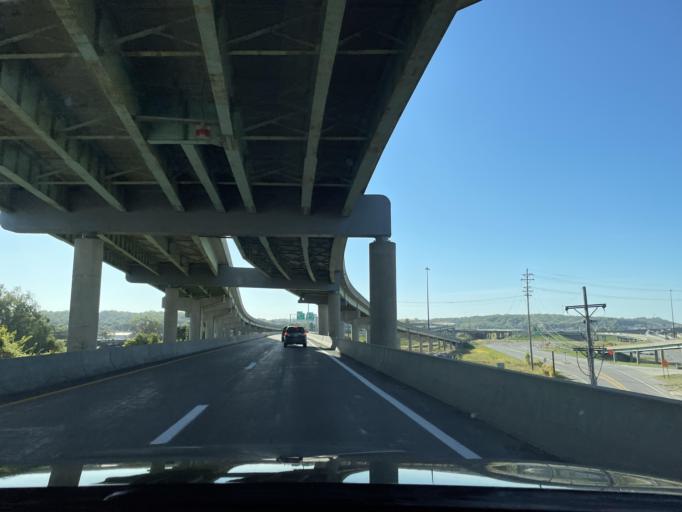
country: US
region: Missouri
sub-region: Buchanan County
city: Saint Joseph
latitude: 39.7542
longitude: -94.8549
